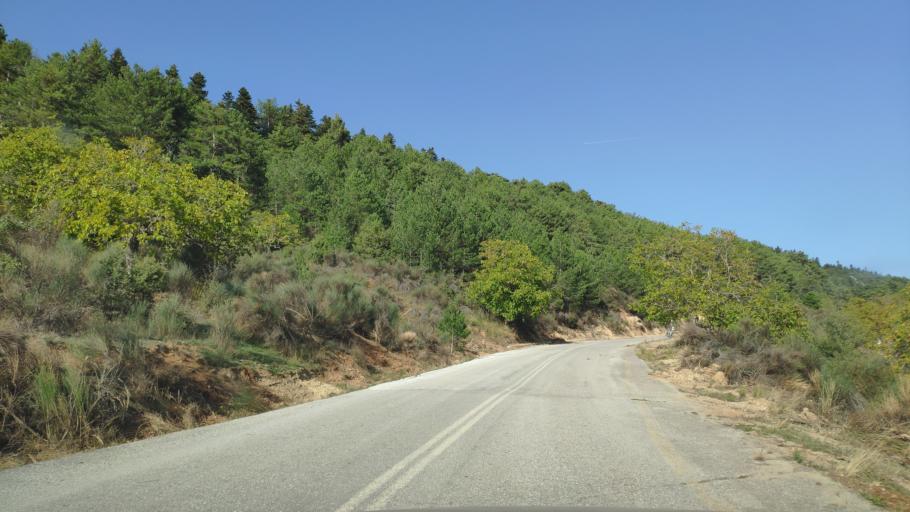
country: GR
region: West Greece
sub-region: Nomos Achaias
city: Aiyira
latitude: 37.9988
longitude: 22.3793
